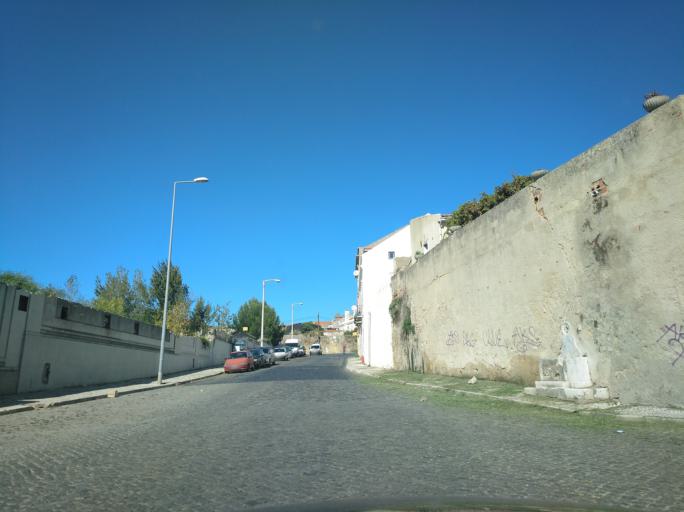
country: PT
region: Lisbon
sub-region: Lisbon
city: Lisbon
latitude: 38.7376
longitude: -9.1074
